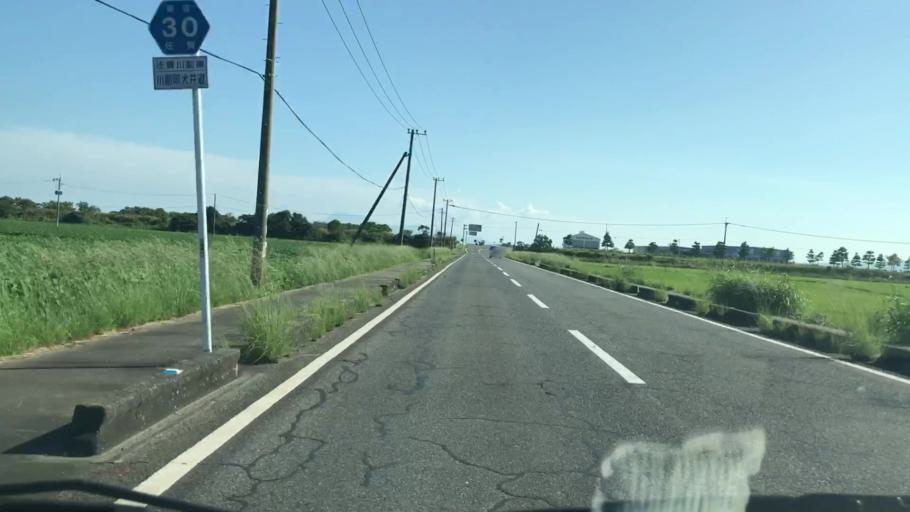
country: JP
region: Saga Prefecture
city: Okawa
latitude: 33.1559
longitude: 130.3080
